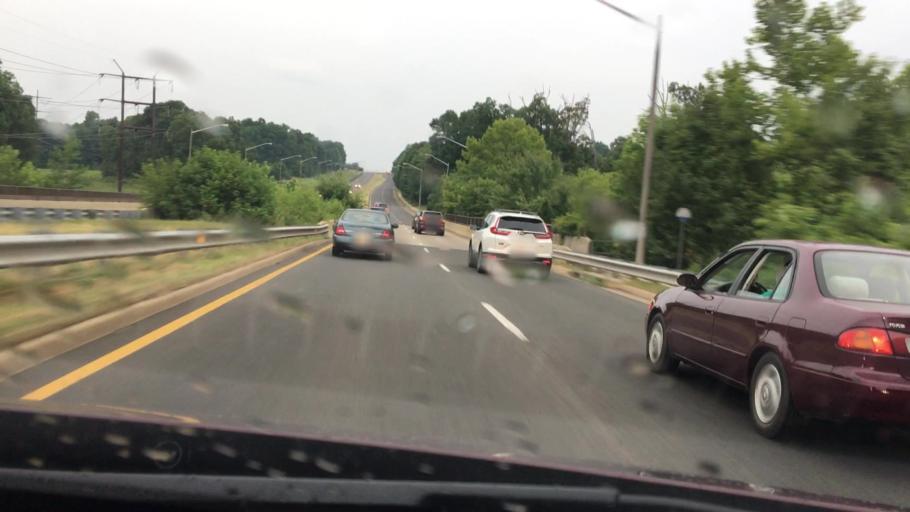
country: US
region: Virginia
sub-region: Fairfax County
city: Centreville
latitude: 38.8298
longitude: -77.4181
